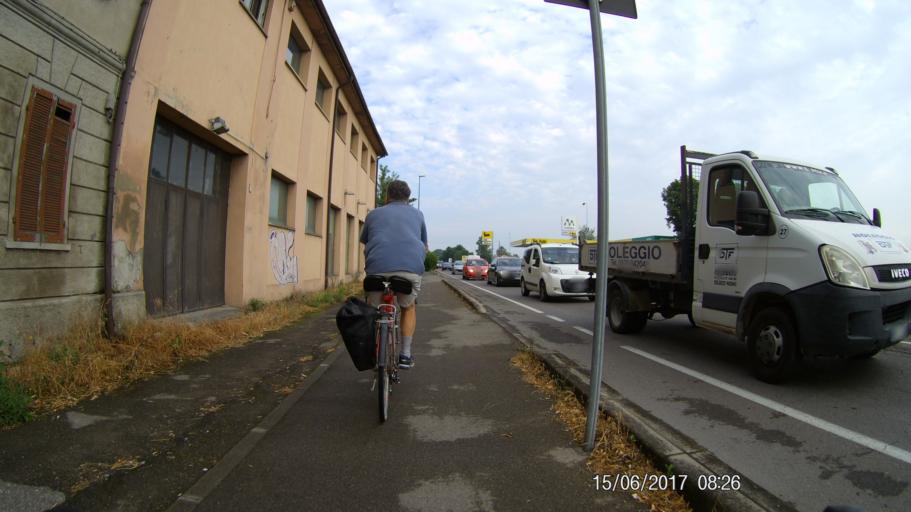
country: IT
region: Emilia-Romagna
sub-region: Provincia di Reggio Emilia
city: Roncocesi
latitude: 44.7235
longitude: 10.5590
